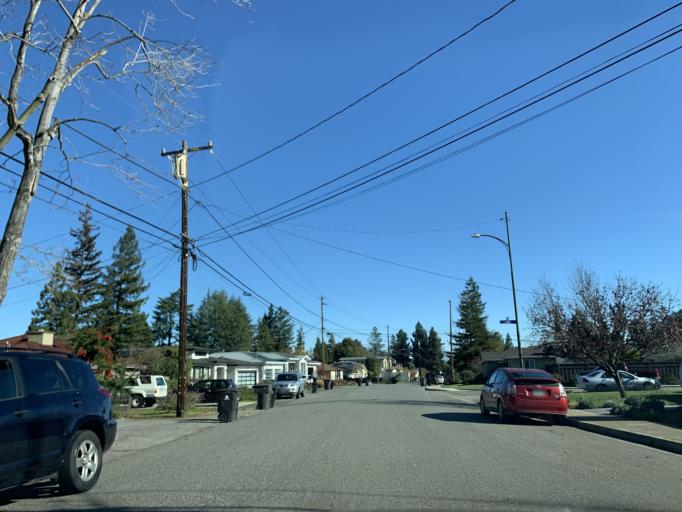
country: US
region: California
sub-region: Santa Clara County
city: Mountain View
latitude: 37.3893
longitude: -122.0988
